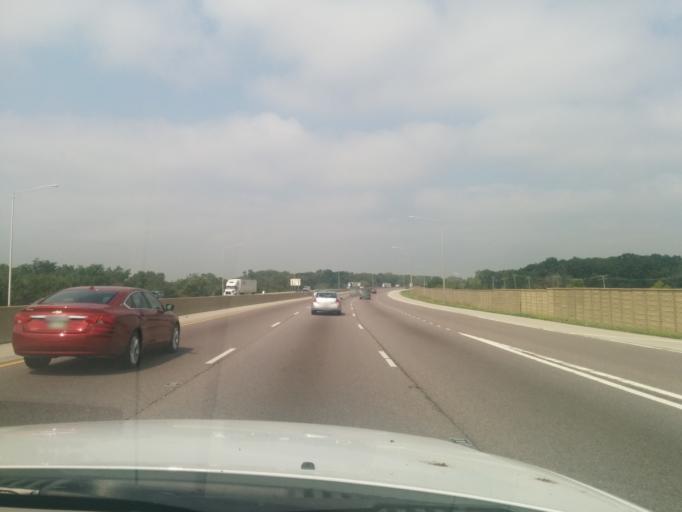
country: US
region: Illinois
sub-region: DuPage County
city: Addison
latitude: 41.9287
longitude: -87.9719
